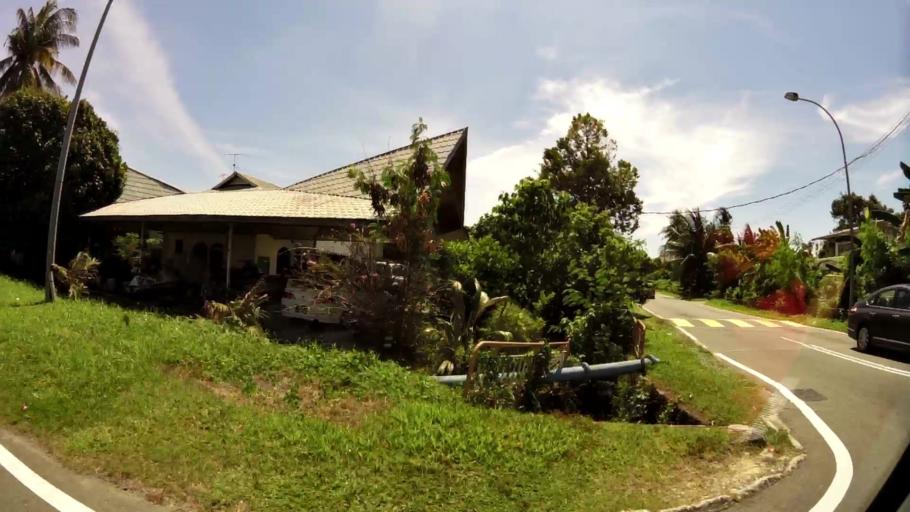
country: BN
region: Brunei and Muara
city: Bandar Seri Begawan
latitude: 4.9402
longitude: 114.9439
